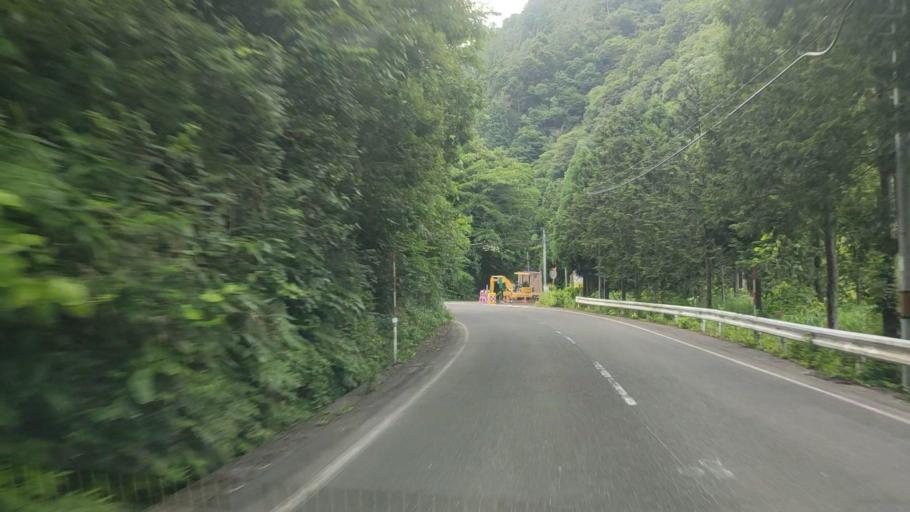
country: JP
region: Tottori
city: Tottori
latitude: 35.3327
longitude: 134.0685
